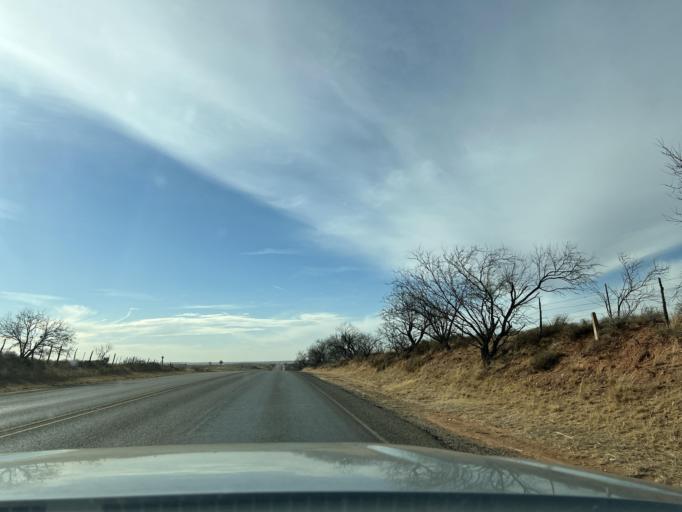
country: US
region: Texas
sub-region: Fisher County
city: Rotan
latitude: 32.7387
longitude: -100.5445
